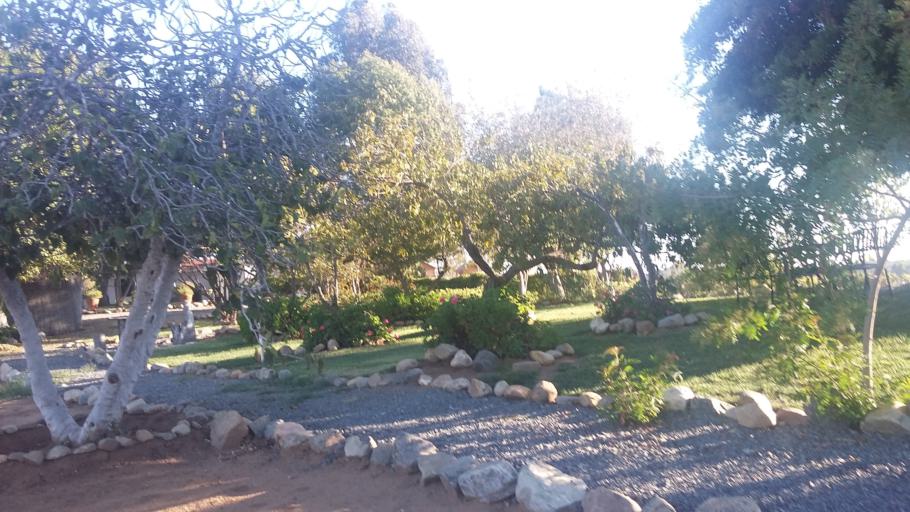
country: MX
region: Baja California
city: El Sauzal
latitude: 32.0022
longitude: -116.6749
